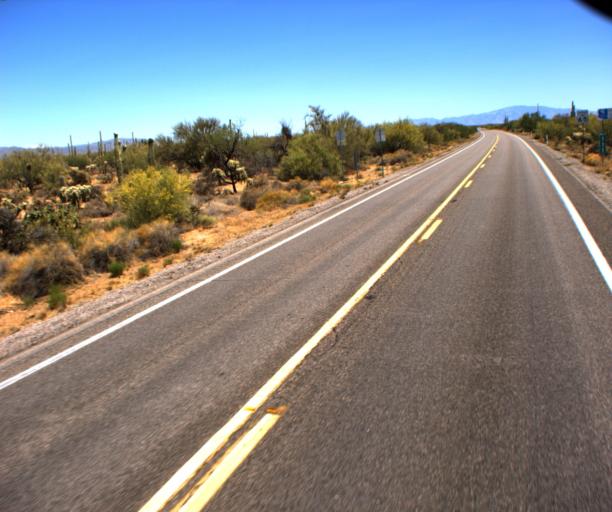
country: US
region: Arizona
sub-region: Pima County
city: Marana
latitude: 32.7689
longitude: -111.1567
